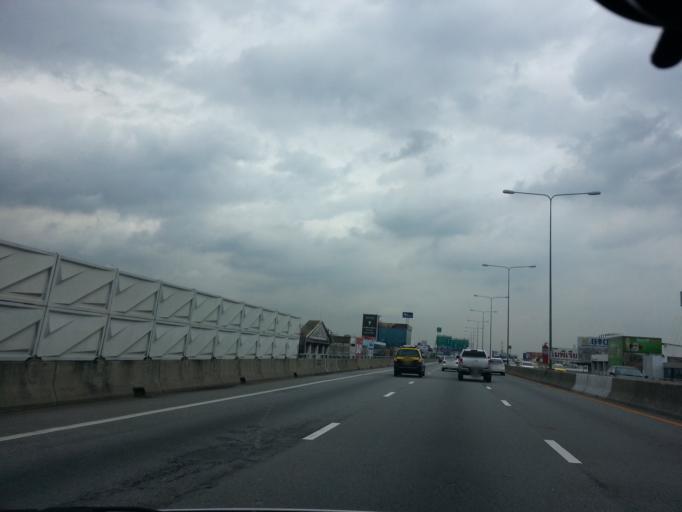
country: TH
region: Bangkok
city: Suan Luang
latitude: 13.7415
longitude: 100.6288
